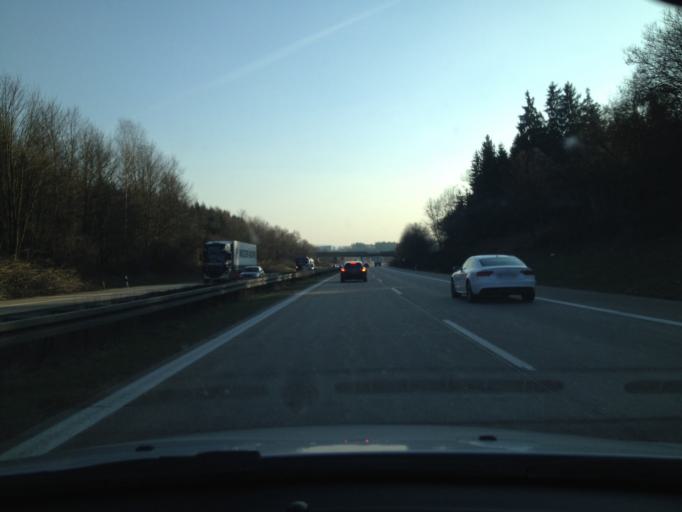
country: DE
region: Baden-Wuerttemberg
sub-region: Regierungsbezirk Stuttgart
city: Ellenberg
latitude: 48.9784
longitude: 10.1923
